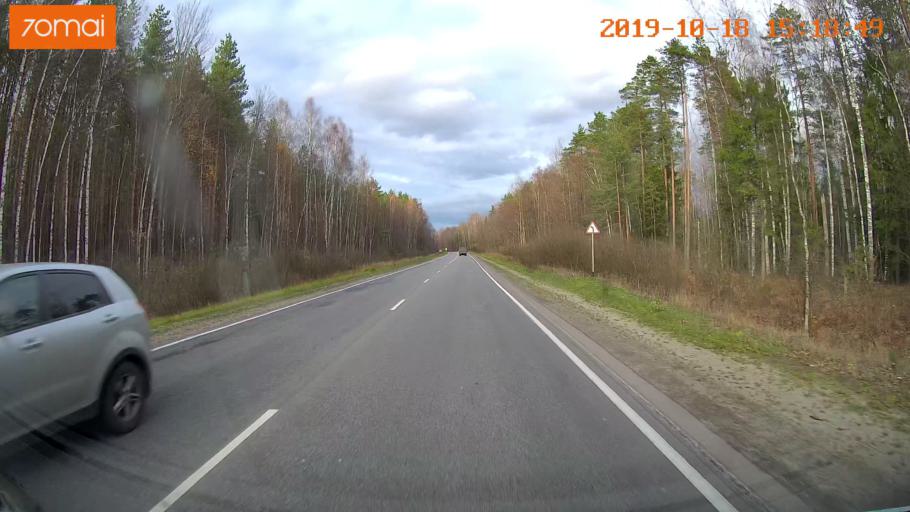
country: RU
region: Vladimir
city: Anopino
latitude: 55.6644
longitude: 40.7326
